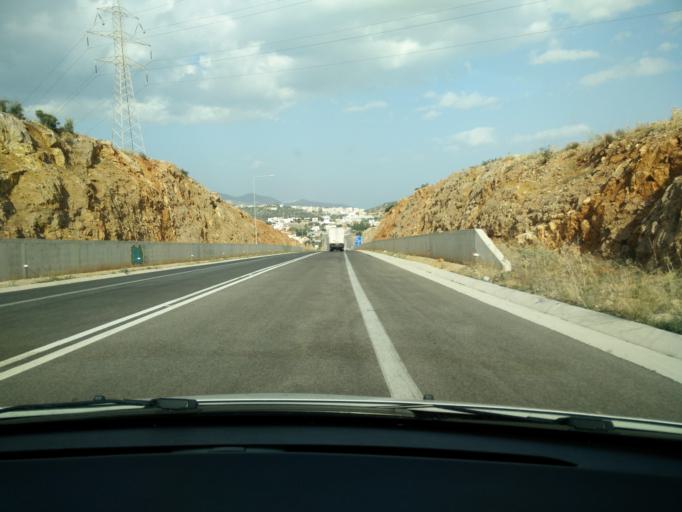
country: GR
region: Crete
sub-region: Nomos Lasithiou
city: Agios Nikolaos
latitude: 35.1791
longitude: 25.7016
